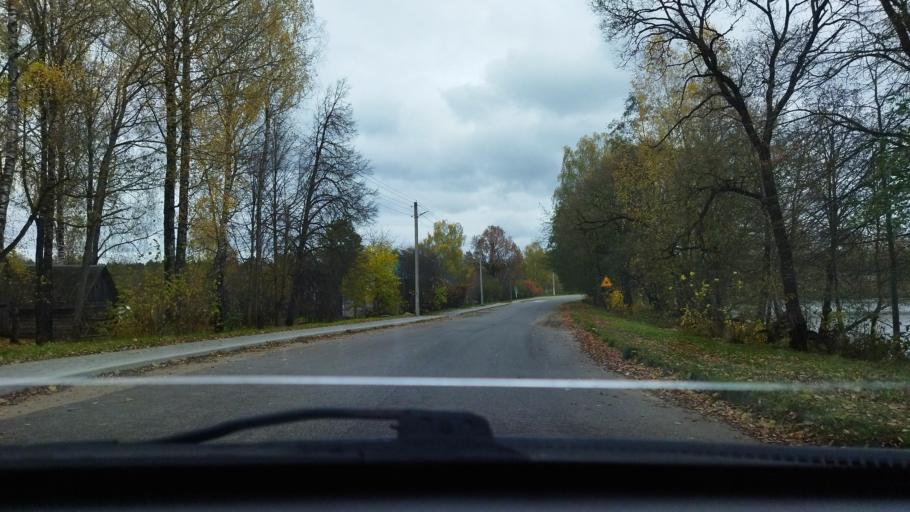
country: BY
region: Minsk
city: Svir
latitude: 54.8073
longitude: 26.2342
